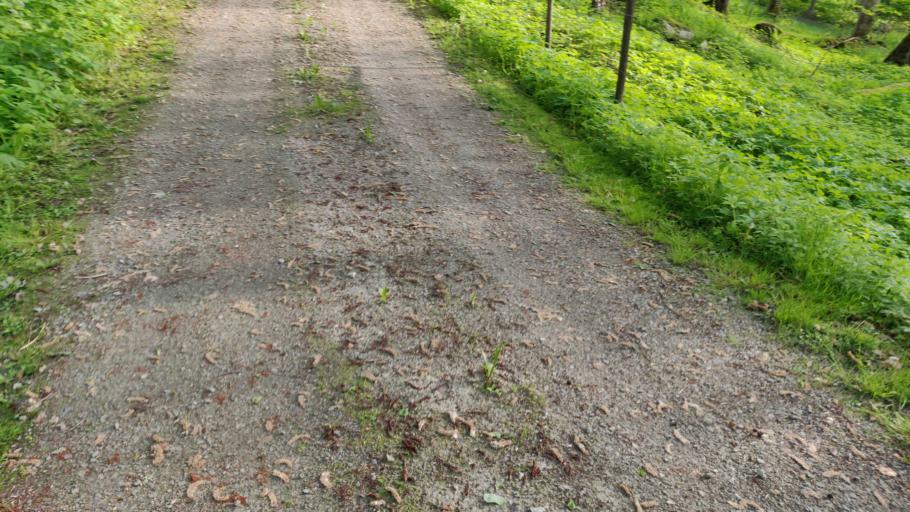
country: SE
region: Vaestra Goetaland
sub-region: Ulricehamns Kommun
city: Ulricehamn
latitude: 57.7804
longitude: 13.3706
